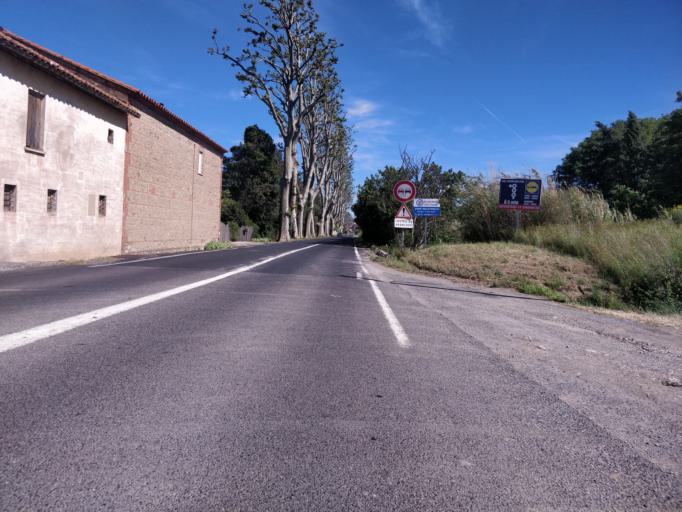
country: FR
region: Languedoc-Roussillon
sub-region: Departement des Pyrenees-Orientales
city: Corneilla-del-Vercol
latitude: 42.6140
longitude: 2.9584
